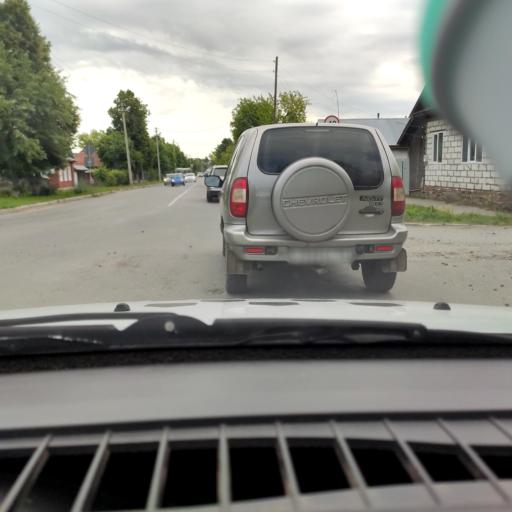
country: RU
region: Sverdlovsk
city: Krasnoufimsk
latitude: 56.6256
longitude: 57.7597
